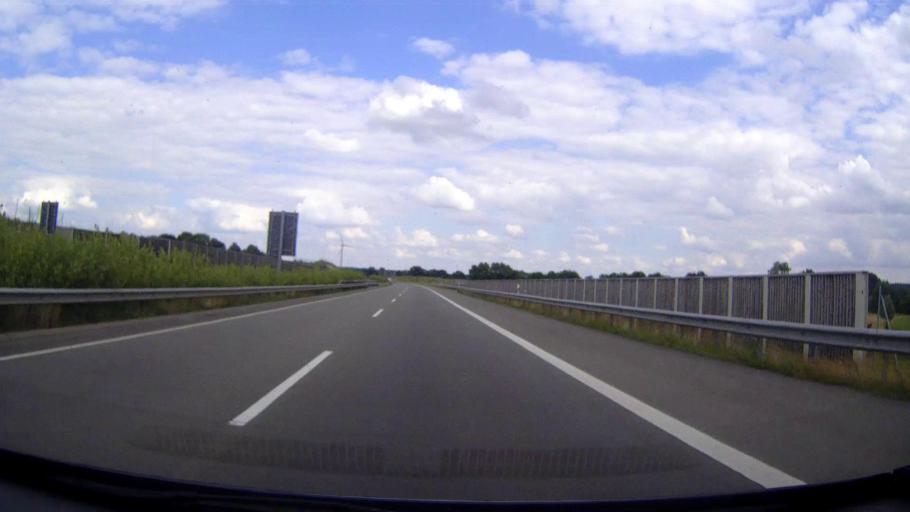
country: DE
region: Schleswig-Holstein
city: Weede
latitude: 53.9179
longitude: 10.4003
